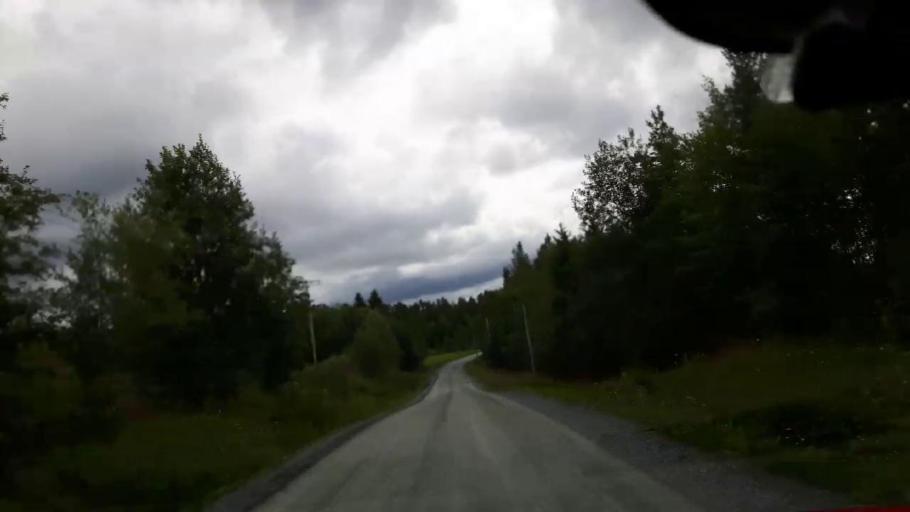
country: SE
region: Jaemtland
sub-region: Krokoms Kommun
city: Krokom
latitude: 63.5740
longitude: 14.2383
